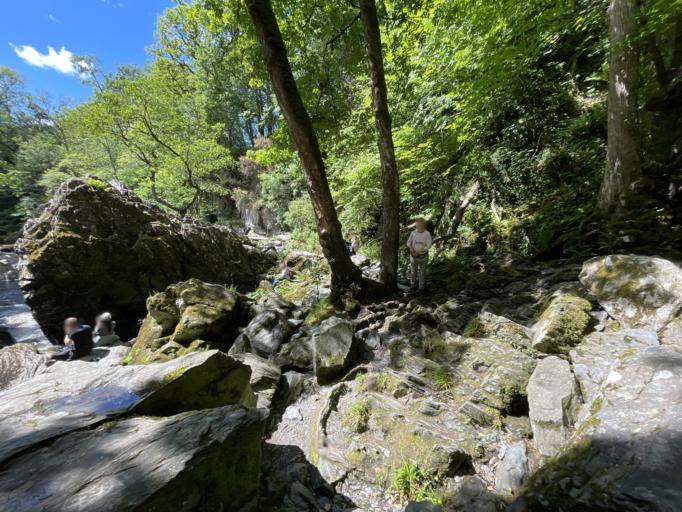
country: GB
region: Wales
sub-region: Conwy
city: Betws-y-Coed
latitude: 53.0727
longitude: -3.7911
